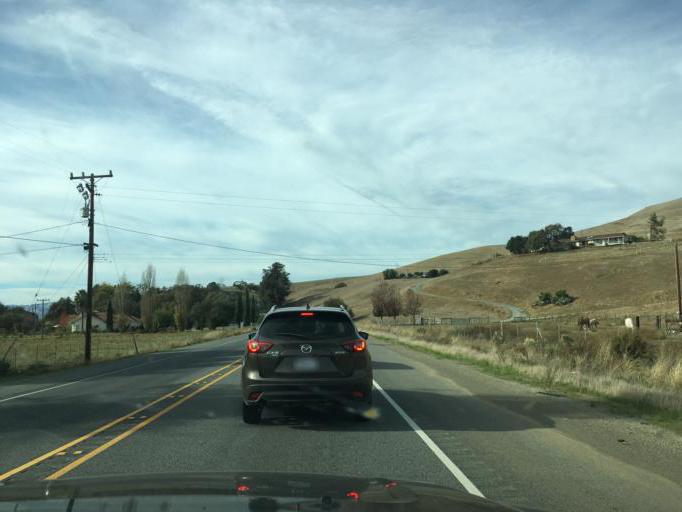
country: US
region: California
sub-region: San Benito County
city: Hollister
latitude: 36.9720
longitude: -121.4222
